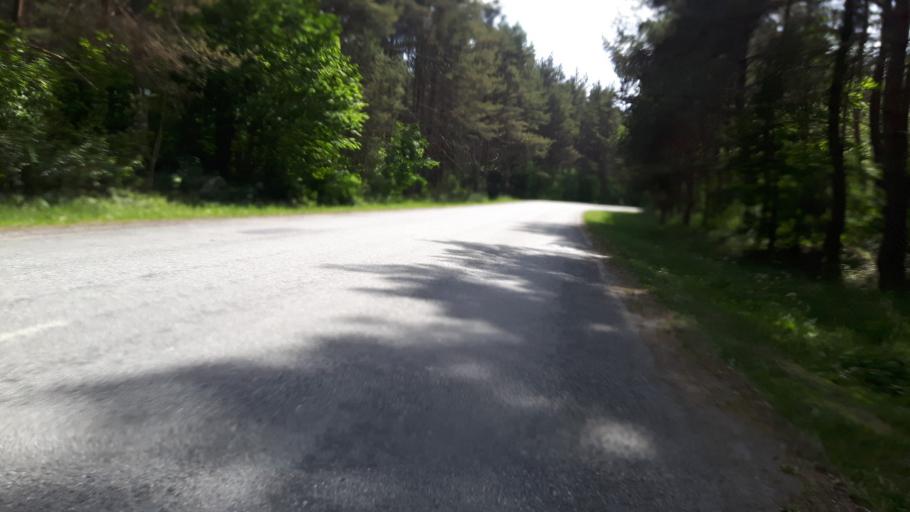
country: EE
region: Harju
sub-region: Raasiku vald
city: Raasiku
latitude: 59.4626
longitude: 25.2376
